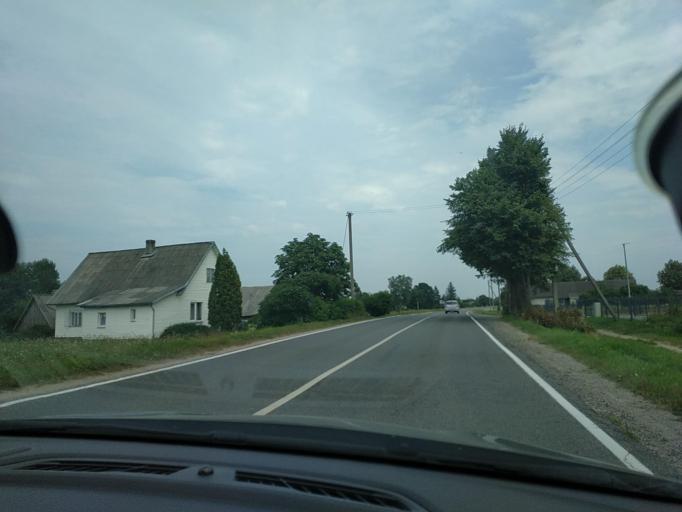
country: LT
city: Nemencine
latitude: 54.8722
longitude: 25.3582
